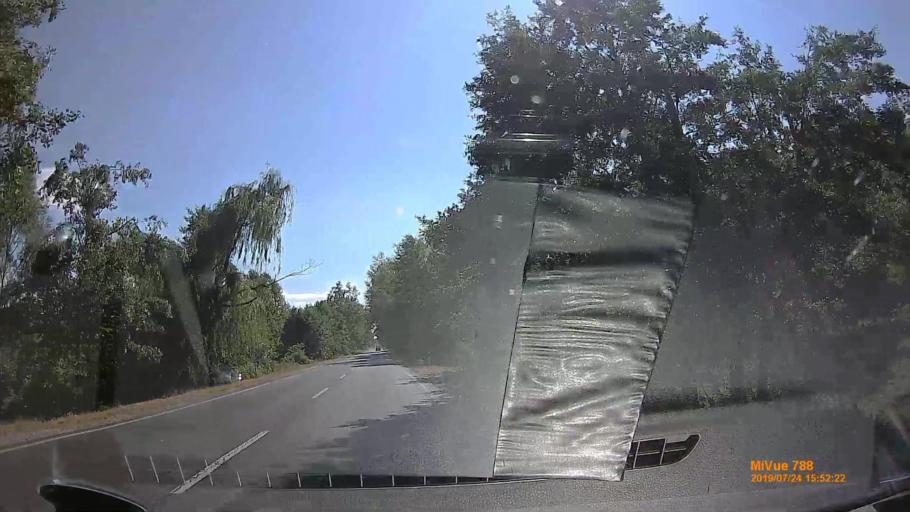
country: HU
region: Szabolcs-Szatmar-Bereg
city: Vaja
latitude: 48.0306
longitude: 22.1671
